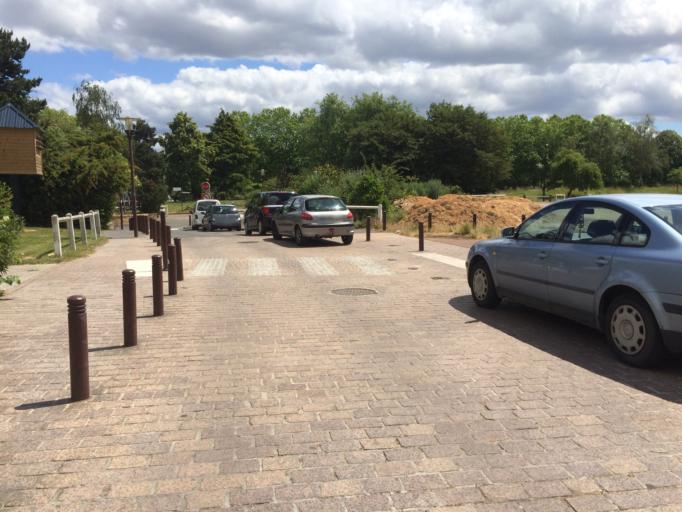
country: FR
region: Ile-de-France
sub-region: Departement de l'Essonne
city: Les Ulis
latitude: 48.6809
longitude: 2.1686
